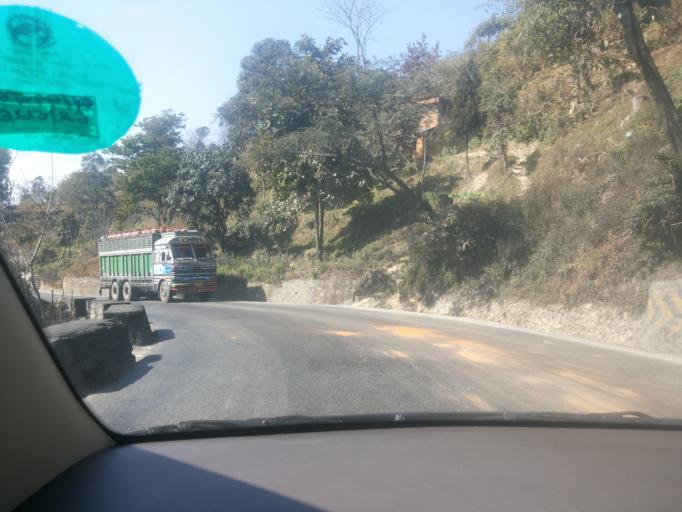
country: NP
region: Central Region
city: Kirtipur
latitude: 27.7142
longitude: 85.2011
